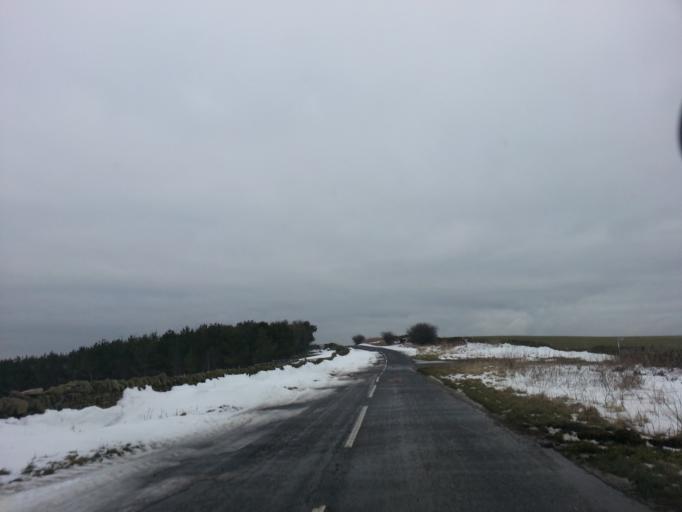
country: GB
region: England
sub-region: County Durham
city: Tow Law
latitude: 54.7687
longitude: -1.8048
